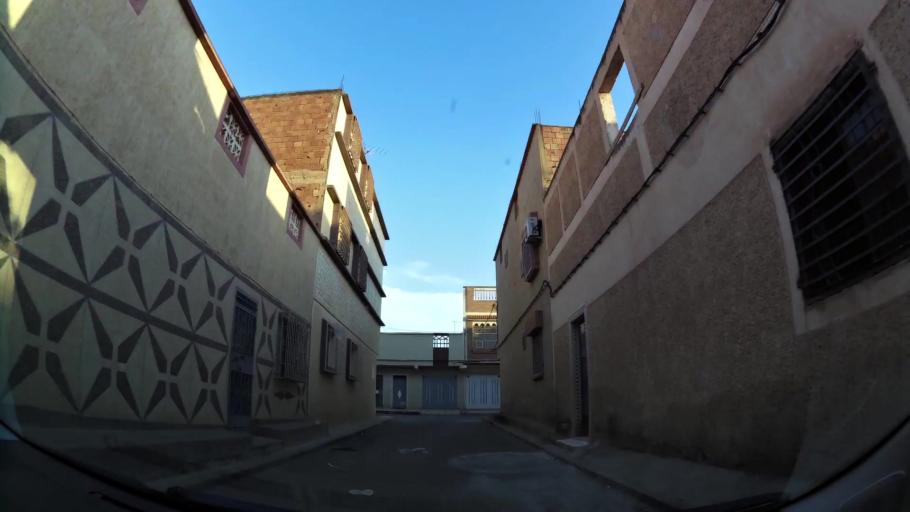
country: MA
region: Oriental
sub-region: Oujda-Angad
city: Oujda
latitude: 34.7093
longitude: -1.9121
